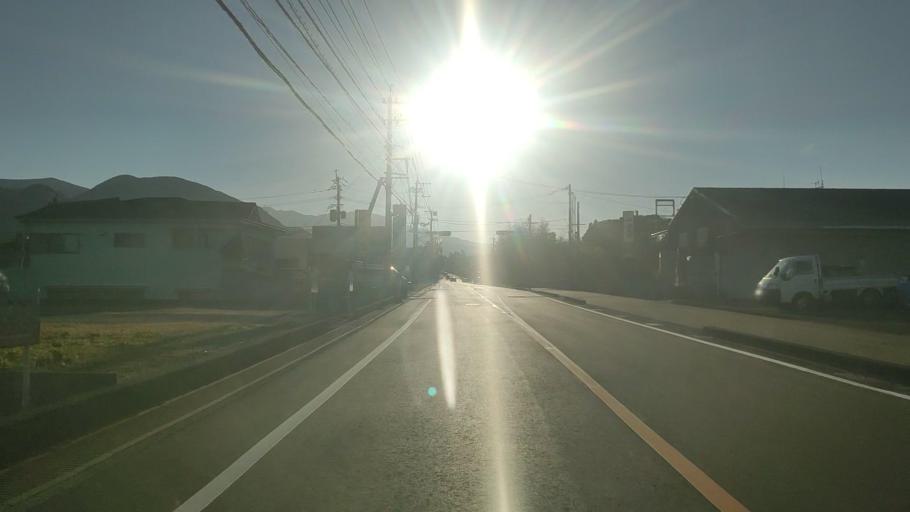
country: JP
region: Miyazaki
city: Miyazaki-shi
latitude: 31.8446
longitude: 131.3437
